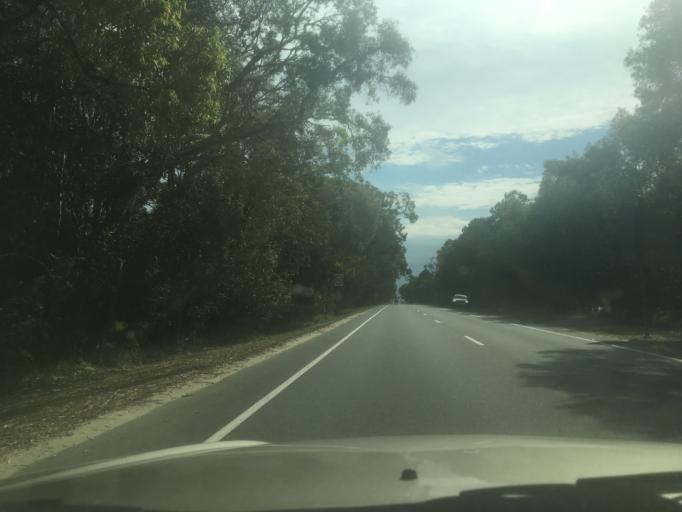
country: AU
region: Queensland
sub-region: Moreton Bay
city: Woorim
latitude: -27.0716
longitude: 153.1986
